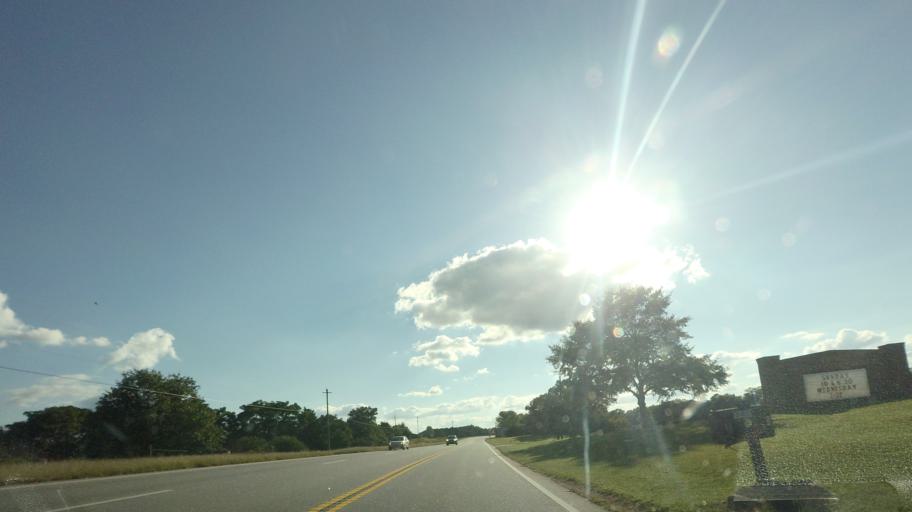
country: US
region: Georgia
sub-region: Upson County
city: Thomaston
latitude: 32.9345
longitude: -84.2588
